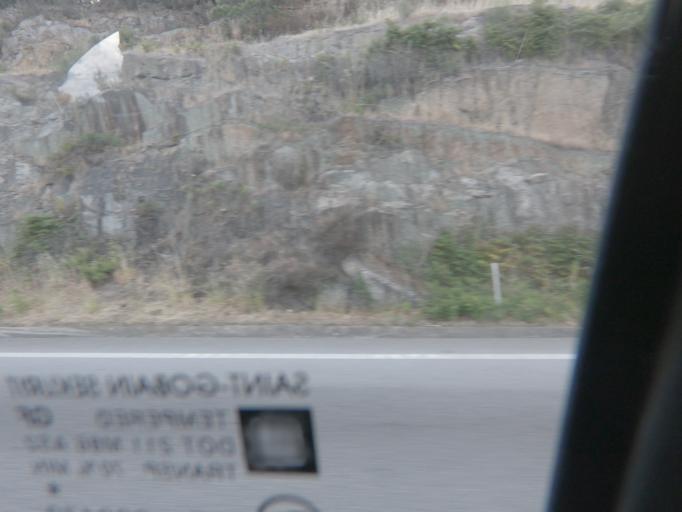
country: PT
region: Porto
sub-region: Paredes
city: Baltar
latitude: 41.1855
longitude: -8.3679
